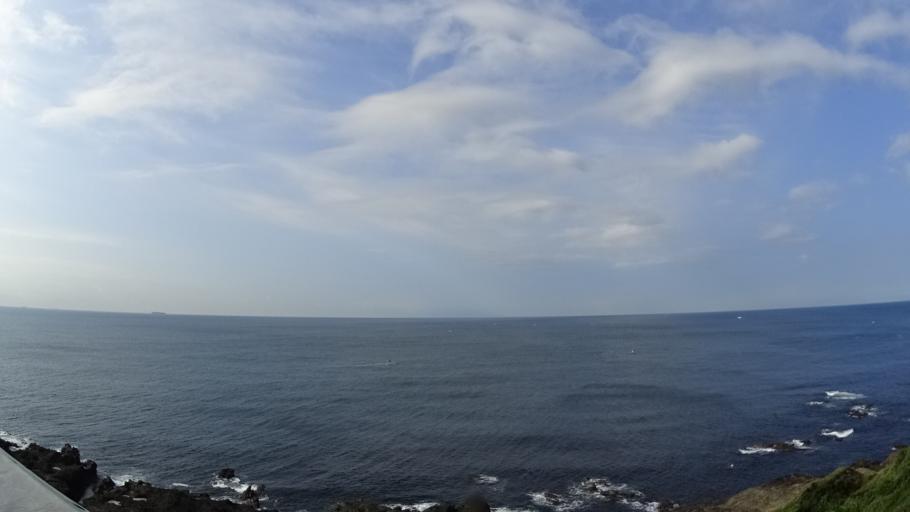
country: JP
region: Kanagawa
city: Miura
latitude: 35.1301
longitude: 139.6273
